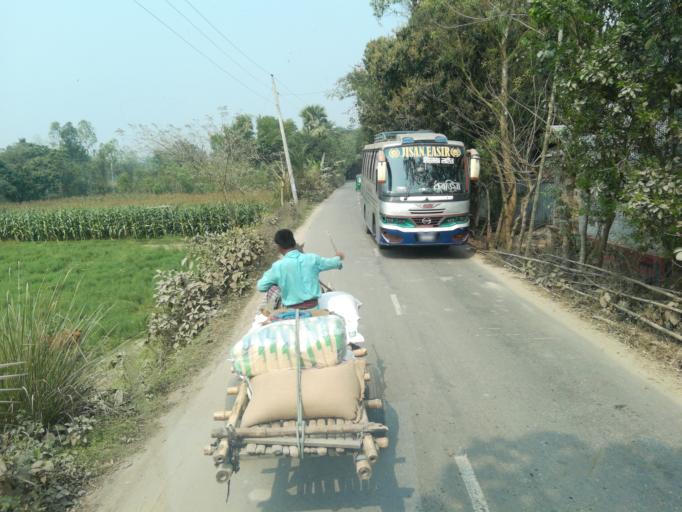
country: BD
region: Dhaka
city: Nagarpur
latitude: 23.9864
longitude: 89.8444
